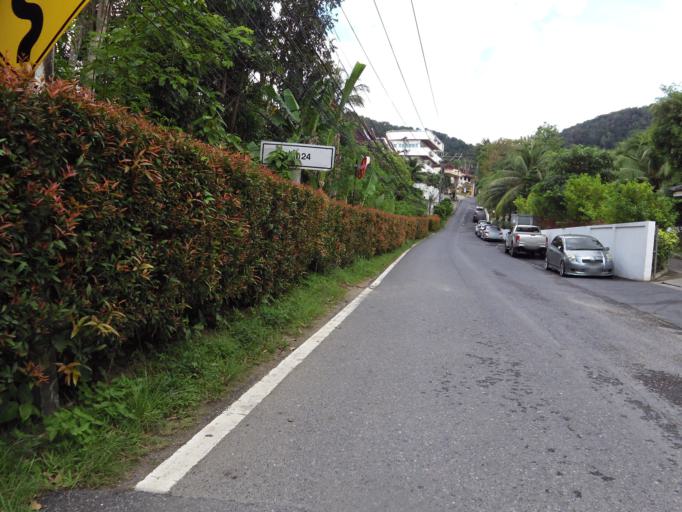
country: TH
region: Phuket
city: Ban Karon
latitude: 7.8556
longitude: 98.2953
